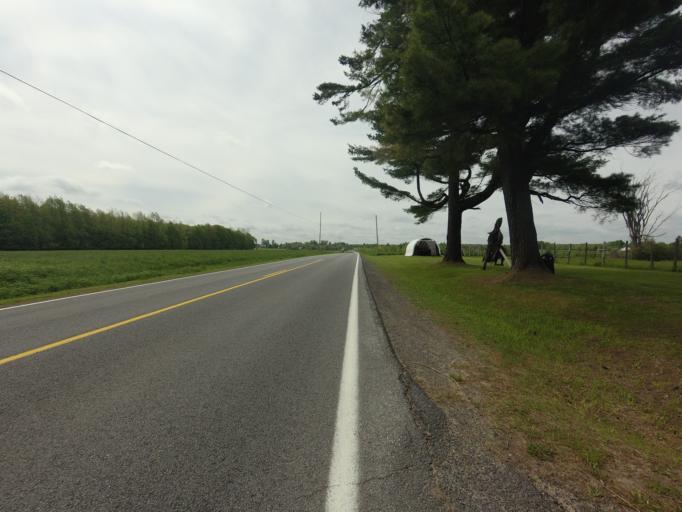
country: CA
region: Ontario
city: Cornwall
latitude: 44.7064
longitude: -74.6597
